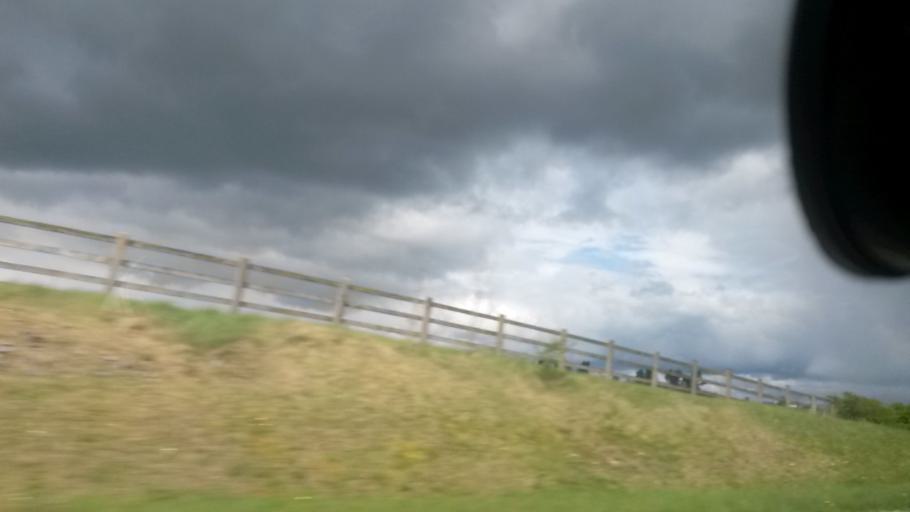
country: IE
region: Leinster
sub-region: Laois
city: Rathdowney
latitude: 52.8564
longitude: -7.4872
